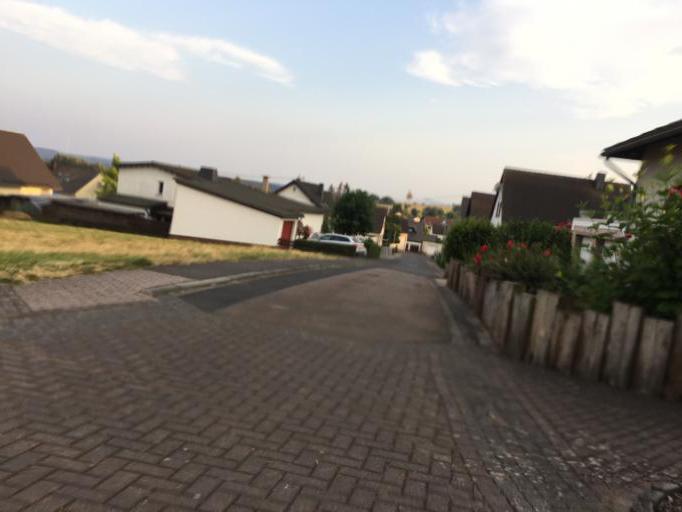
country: DE
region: Rheinland-Pfalz
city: Weroth
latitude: 50.4617
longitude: 7.9486
